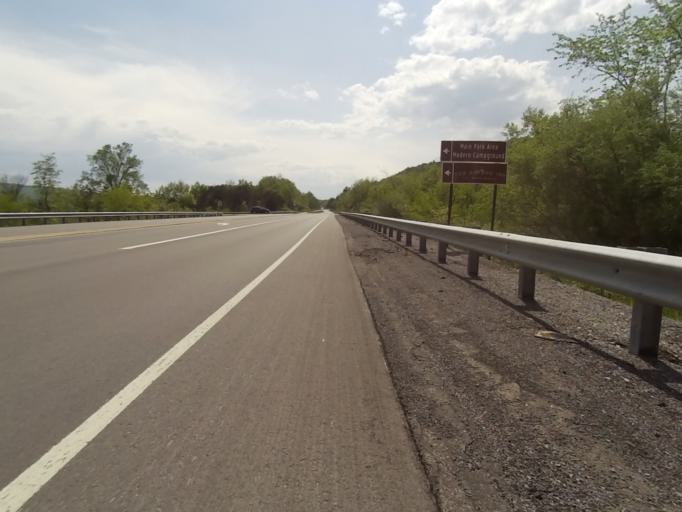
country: US
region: Pennsylvania
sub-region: Centre County
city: Zion
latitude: 41.0367
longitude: -77.6508
